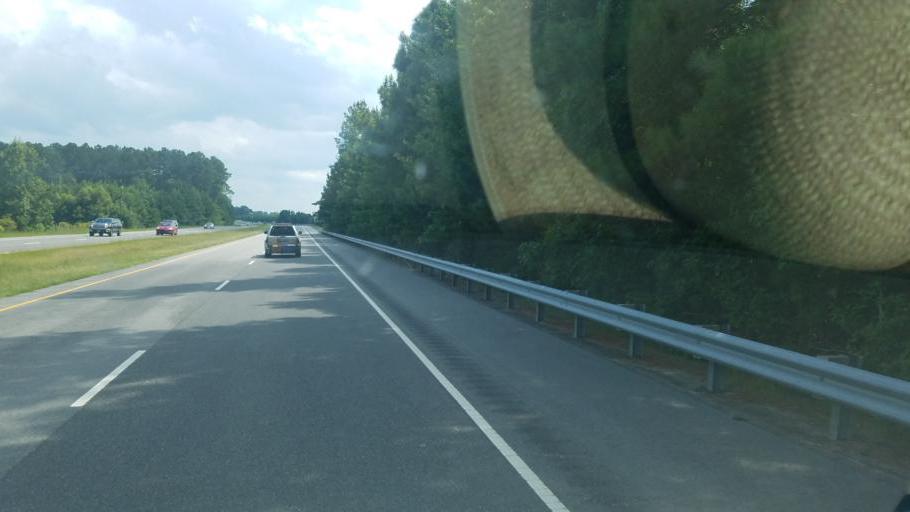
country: US
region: North Carolina
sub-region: Currituck County
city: Moyock
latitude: 36.6269
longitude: -76.2150
